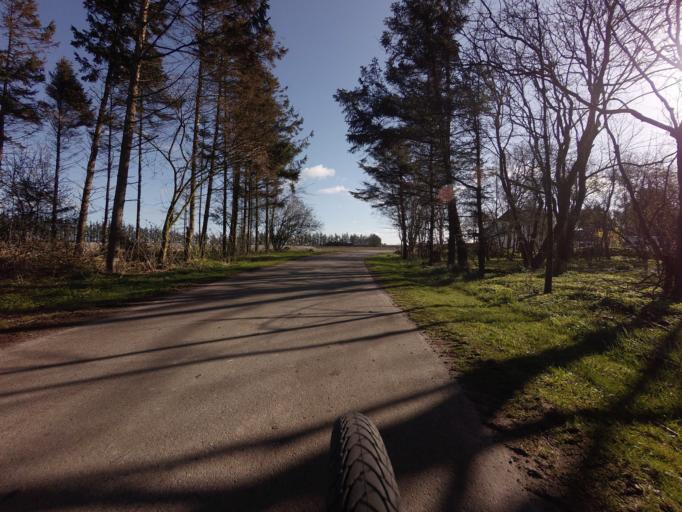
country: DK
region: North Denmark
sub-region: Hjorring Kommune
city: Vra
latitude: 57.3607
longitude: 9.8208
